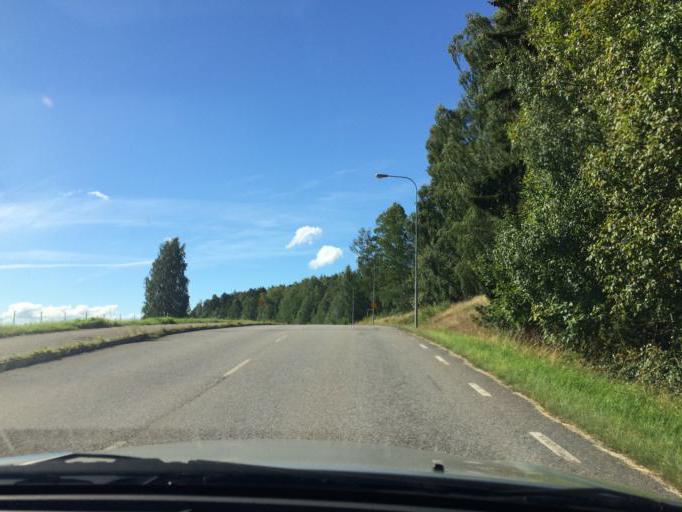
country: SE
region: Vaestmanland
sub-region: Vasteras
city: Vasteras
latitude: 59.5977
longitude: 16.6243
